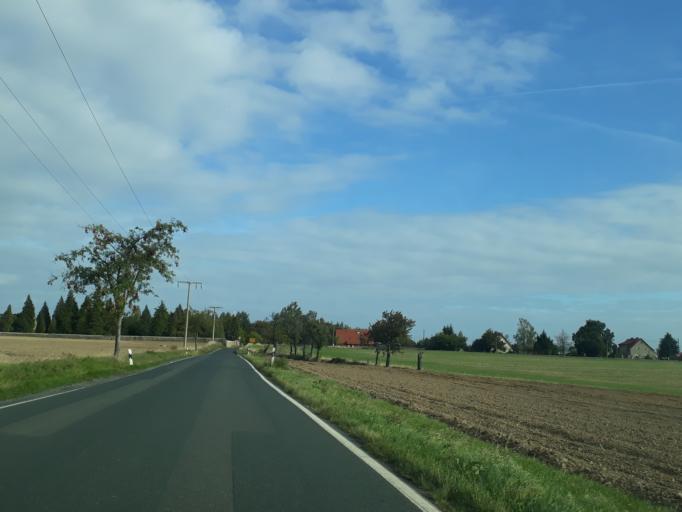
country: DE
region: Saxony
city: Klipphausen
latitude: 51.0813
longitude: 13.5811
